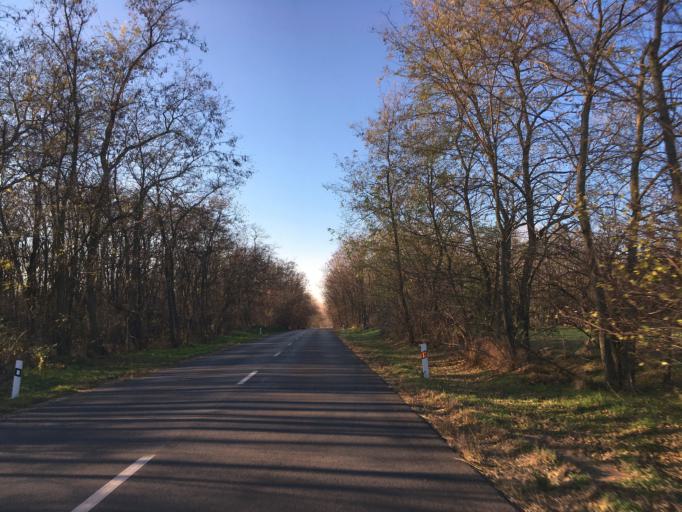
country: SK
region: Nitriansky
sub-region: Okres Komarno
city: Hurbanovo
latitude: 47.8976
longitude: 18.1668
